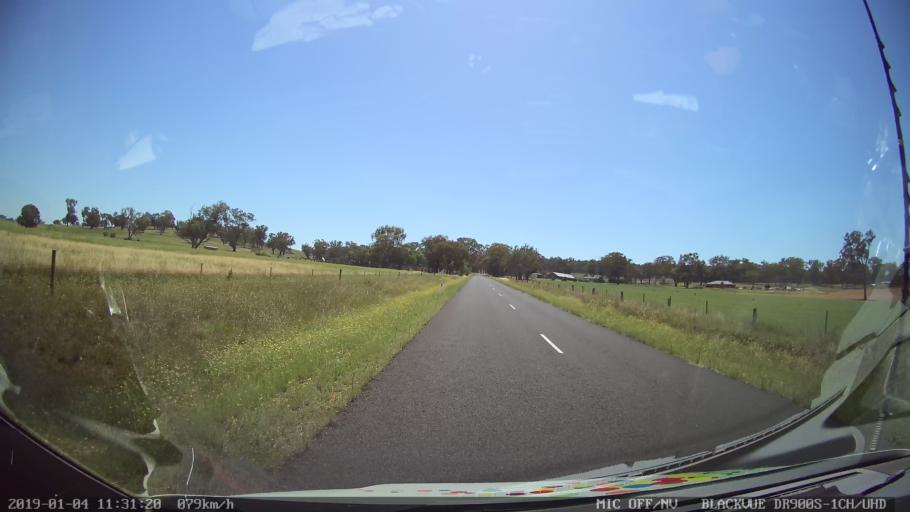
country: AU
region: New South Wales
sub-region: Cabonne
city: Molong
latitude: -33.0728
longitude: 148.7922
